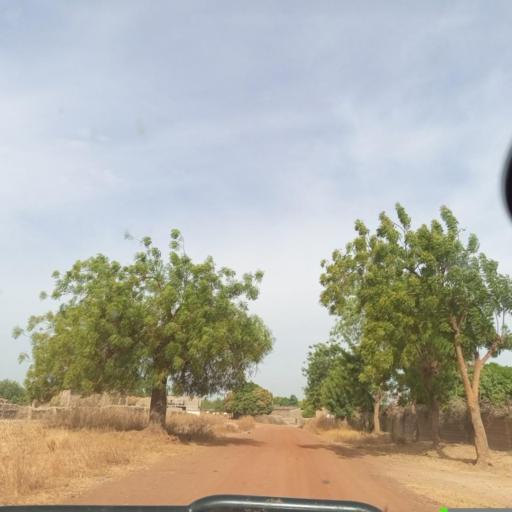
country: ML
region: Koulikoro
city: Koulikoro
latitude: 13.1100
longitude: -7.6505
